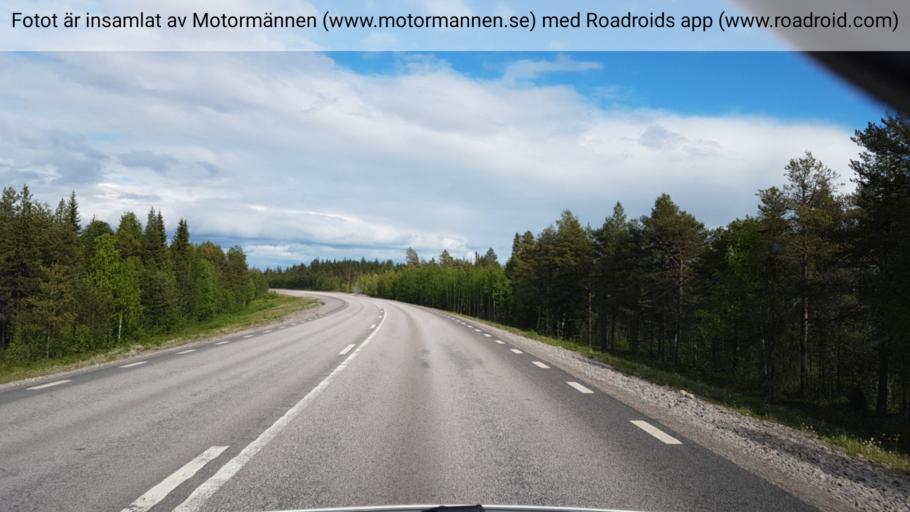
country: SE
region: Norrbotten
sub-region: Gallivare Kommun
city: Malmberget
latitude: 67.6575
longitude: 21.5354
